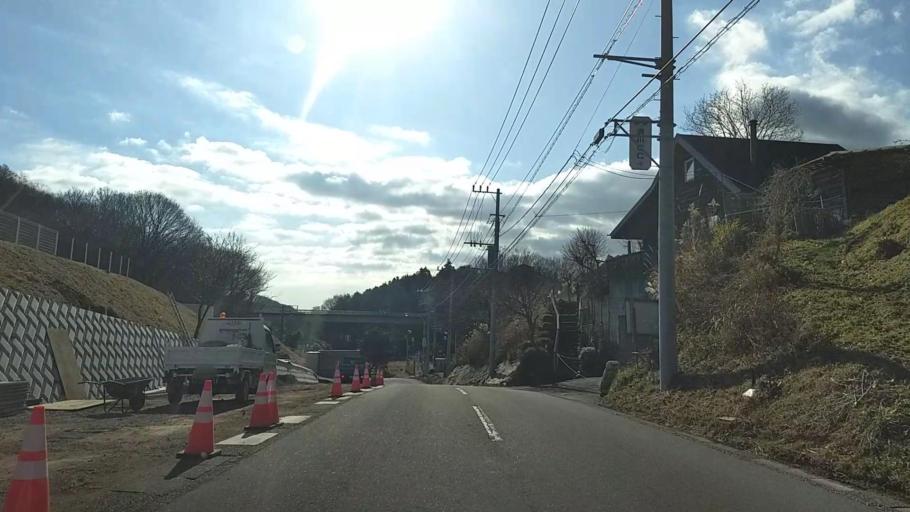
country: JP
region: Kanagawa
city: Atsugi
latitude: 35.4661
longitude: 139.2884
